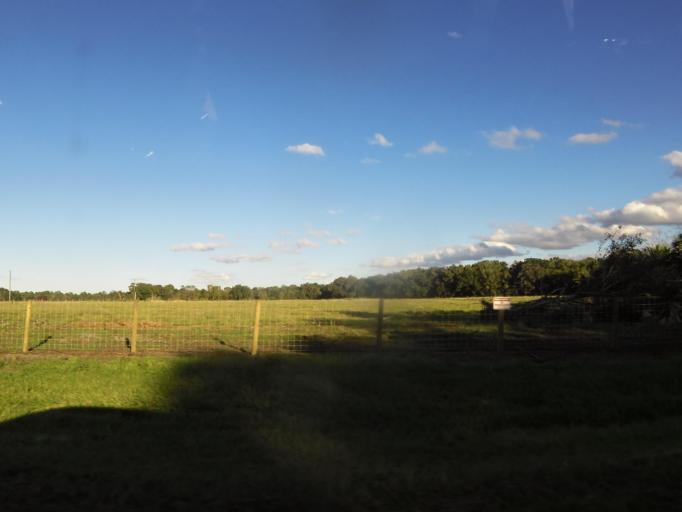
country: US
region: Florida
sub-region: Marion County
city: Citra
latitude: 29.4593
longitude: -82.1056
